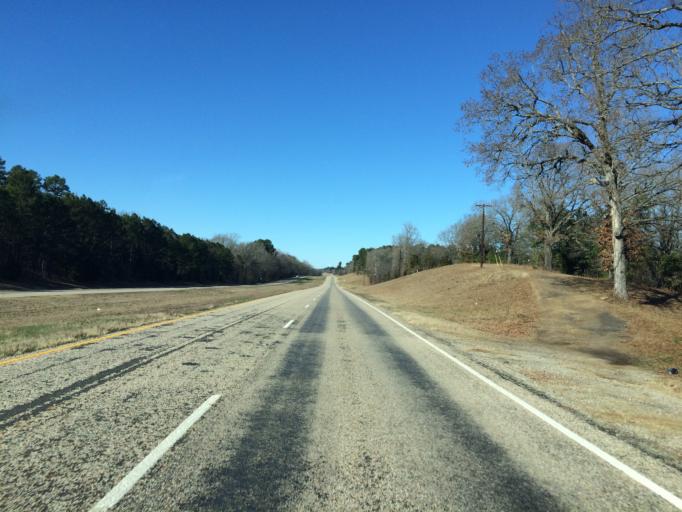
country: US
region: Texas
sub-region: Wood County
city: Mineola
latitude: 32.6448
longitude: -95.4020
